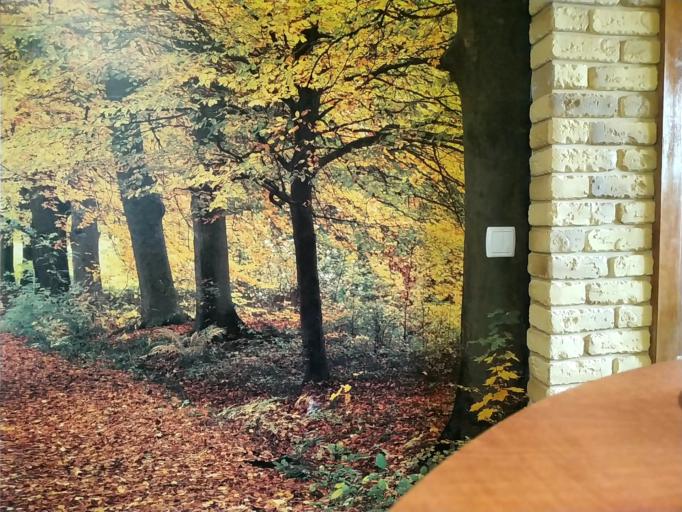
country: RU
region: Novgorod
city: Opechenskiy Posad
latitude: 58.2699
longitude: 34.0125
